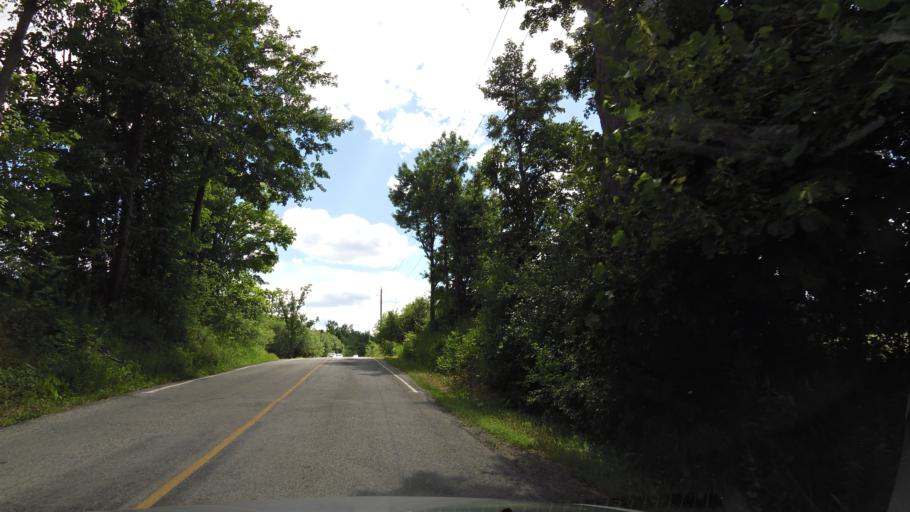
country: CA
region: Ontario
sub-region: Halton
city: Milton
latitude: 43.5955
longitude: -79.9087
